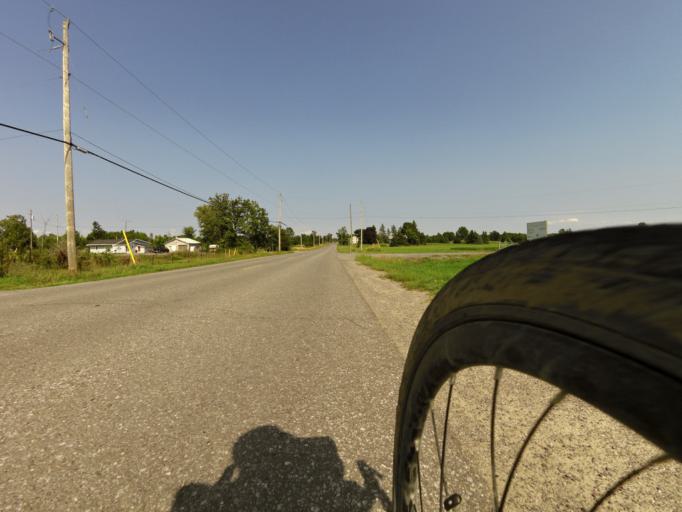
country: CA
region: Ontario
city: Skatepark
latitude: 44.2452
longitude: -76.7298
